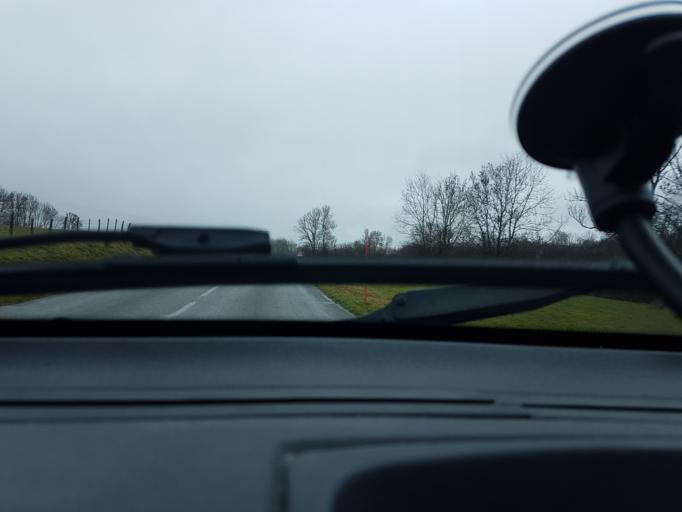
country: FR
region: Franche-Comte
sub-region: Departement du Doubs
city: Valdahon
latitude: 47.1038
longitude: 6.3559
